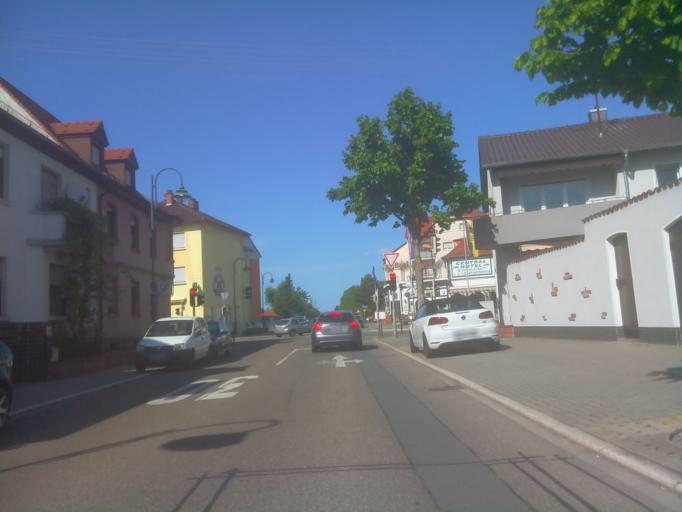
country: DE
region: Baden-Wuerttemberg
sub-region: Karlsruhe Region
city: Schwetzingen
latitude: 49.3903
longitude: 8.5697
